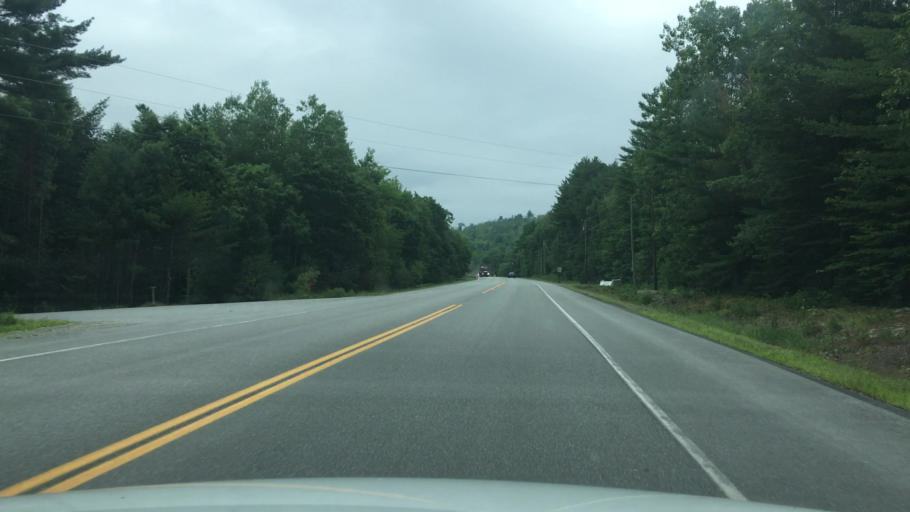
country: US
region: Maine
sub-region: Penobscot County
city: Bradley
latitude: 44.8248
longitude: -68.4857
